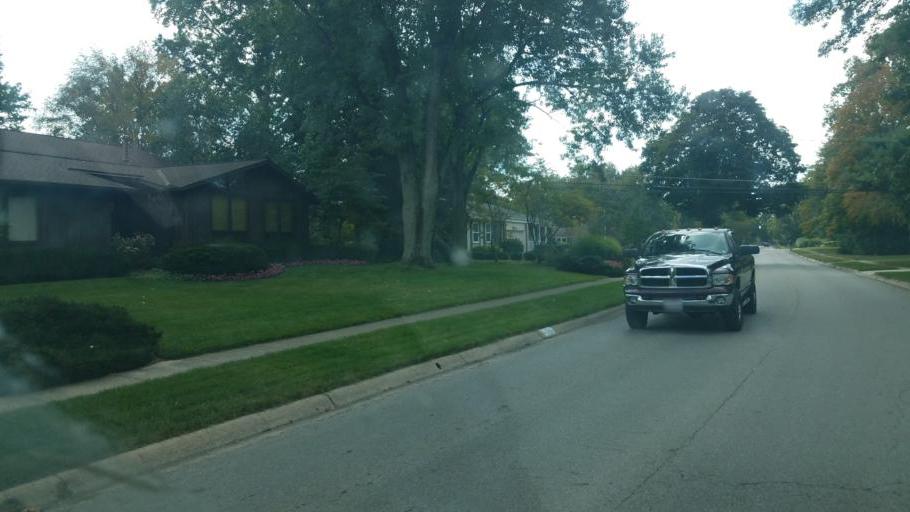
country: US
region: Ohio
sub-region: Franklin County
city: Worthington
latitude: 40.1066
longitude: -83.0280
